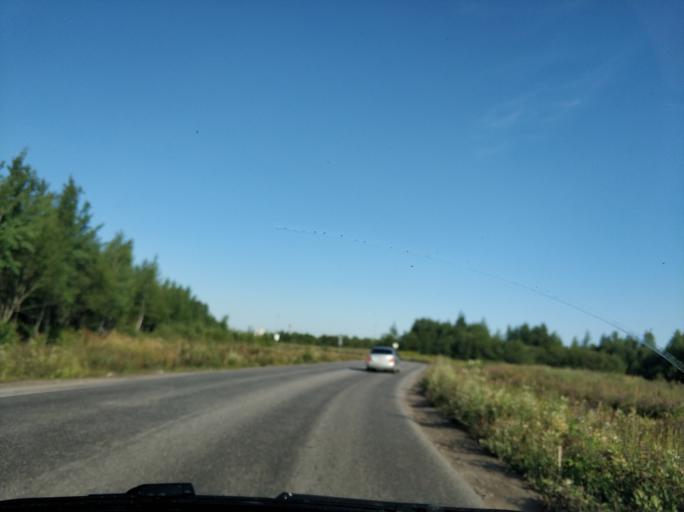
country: RU
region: St.-Petersburg
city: Grazhdanka
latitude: 60.0493
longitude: 30.4042
